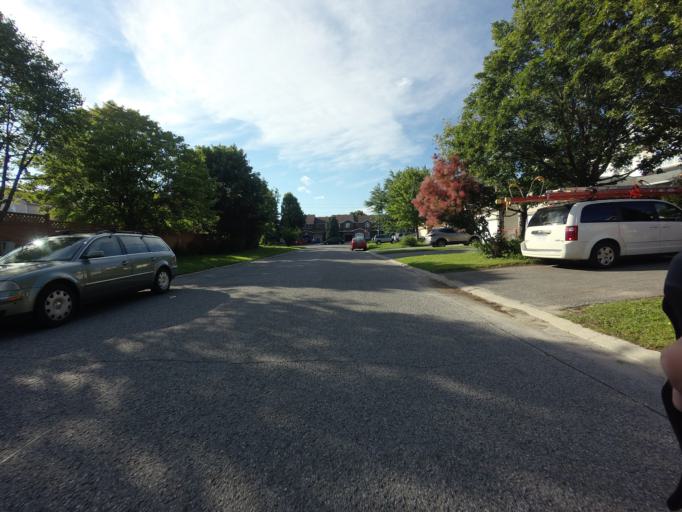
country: CA
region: Ontario
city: Bells Corners
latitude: 45.2959
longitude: -75.7345
